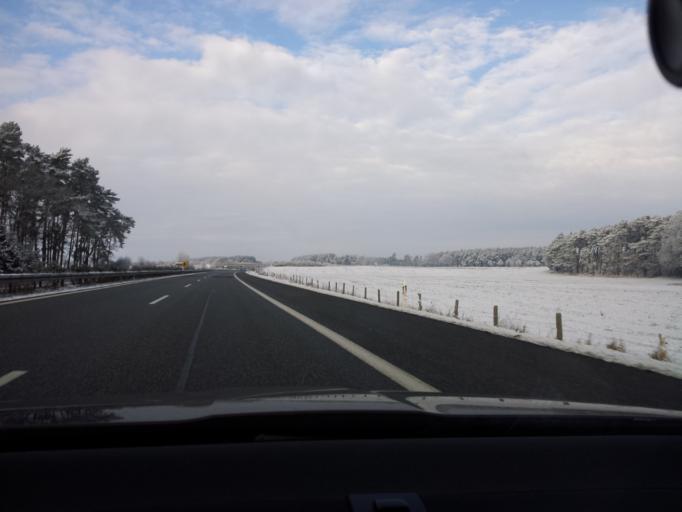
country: DE
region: Mecklenburg-Vorpommern
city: Locknitz
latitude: 53.3520
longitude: 11.7805
